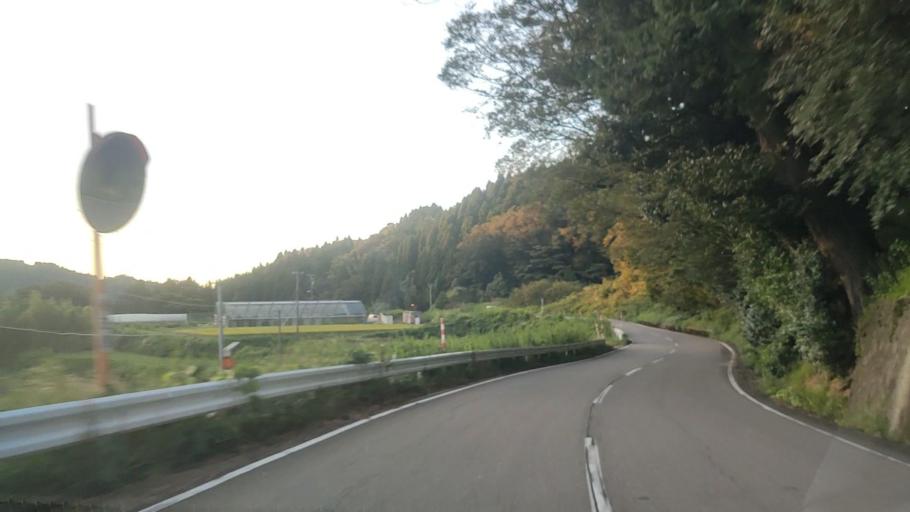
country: JP
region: Ishikawa
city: Tsubata
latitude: 36.6248
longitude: 136.7788
